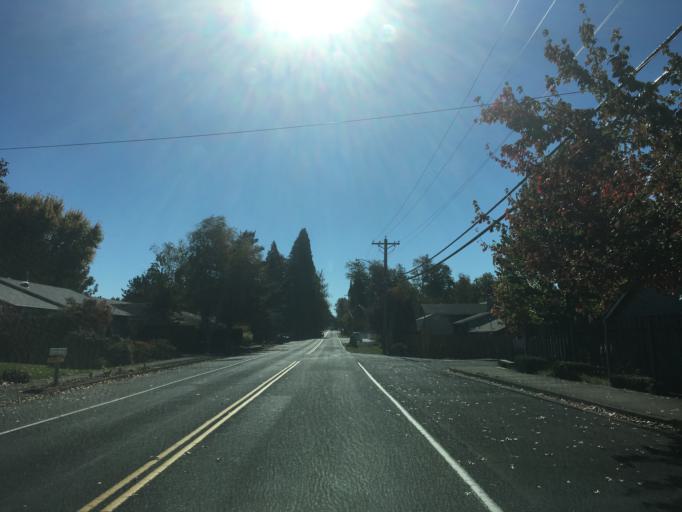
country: US
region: Oregon
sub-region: Multnomah County
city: Gresham
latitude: 45.4844
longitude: -122.4036
